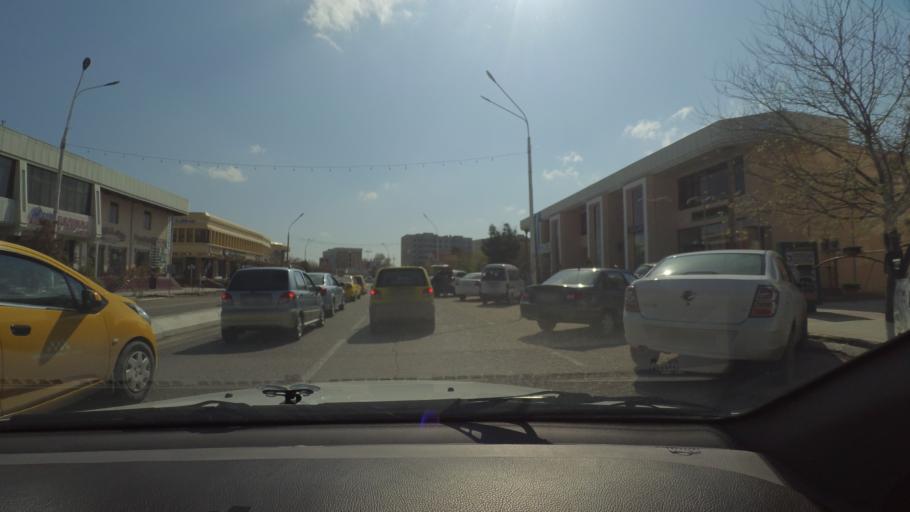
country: UZ
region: Bukhara
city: Bukhara
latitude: 39.7719
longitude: 64.4311
